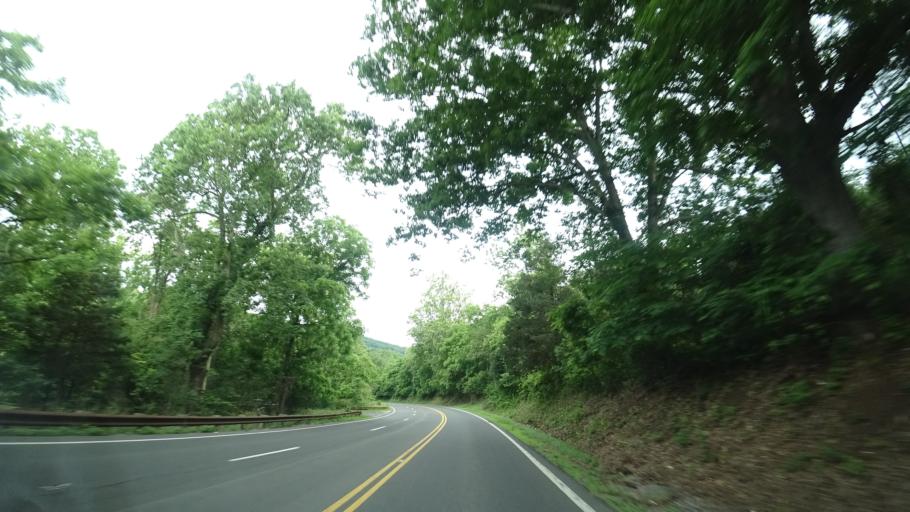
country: US
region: Virginia
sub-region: Page County
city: Luray
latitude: 38.6582
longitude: -78.3657
